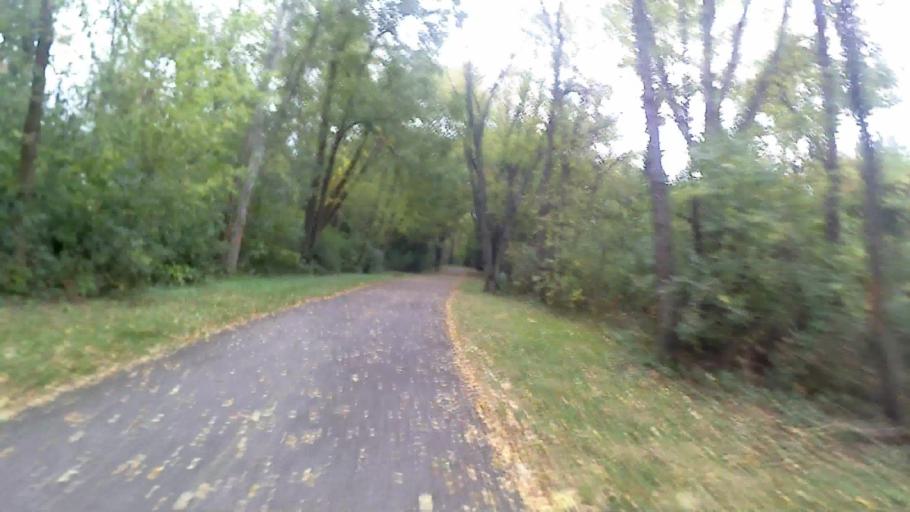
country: US
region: Illinois
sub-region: Kane County
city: Montgomery
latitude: 41.7500
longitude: -88.3723
